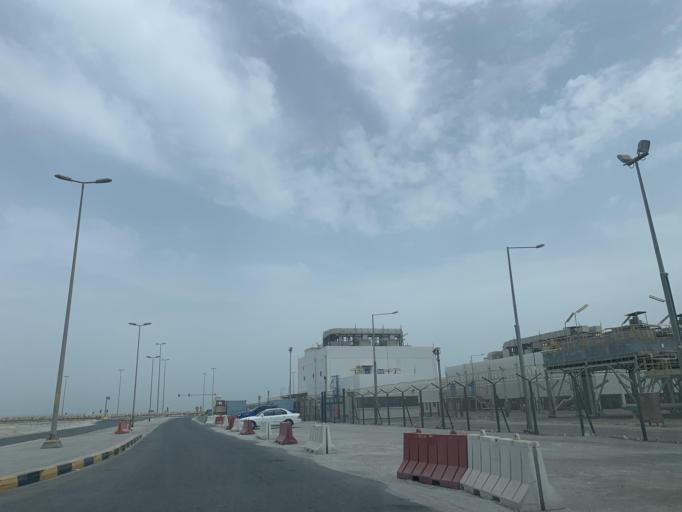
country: BH
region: Muharraq
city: Al Hadd
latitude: 26.2102
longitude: 50.7018
